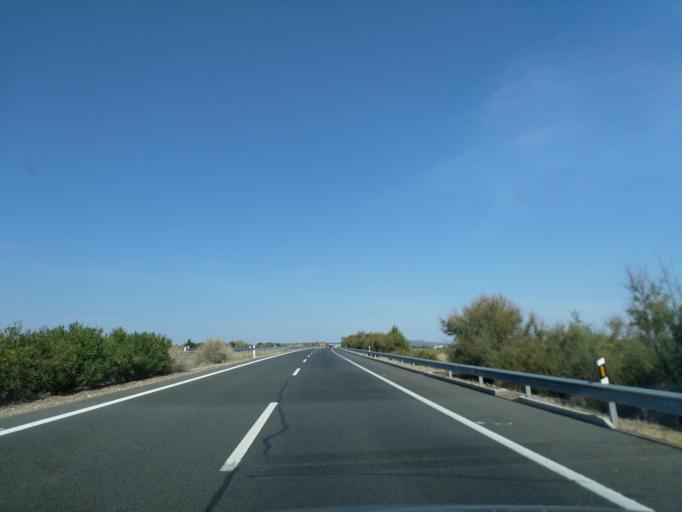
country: ES
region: Extremadura
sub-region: Provincia de Caceres
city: Aldea del Cano
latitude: 39.3211
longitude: -6.3294
